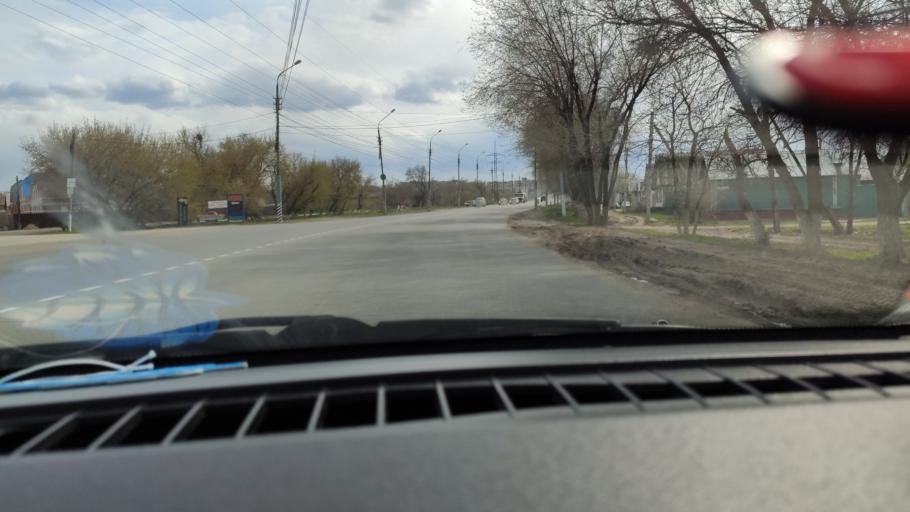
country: RU
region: Saratov
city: Privolzhskiy
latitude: 51.4178
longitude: 46.0457
